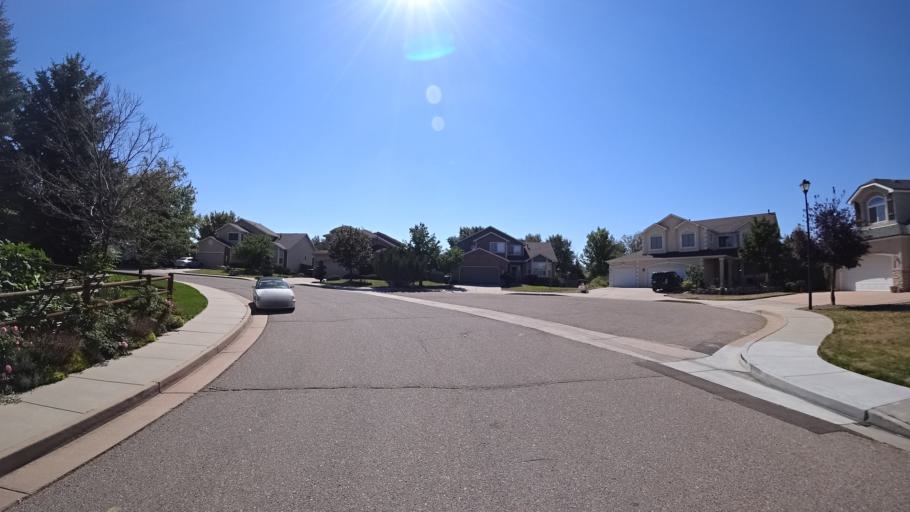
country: US
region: Colorado
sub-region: El Paso County
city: Black Forest
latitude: 38.9602
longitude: -104.7426
